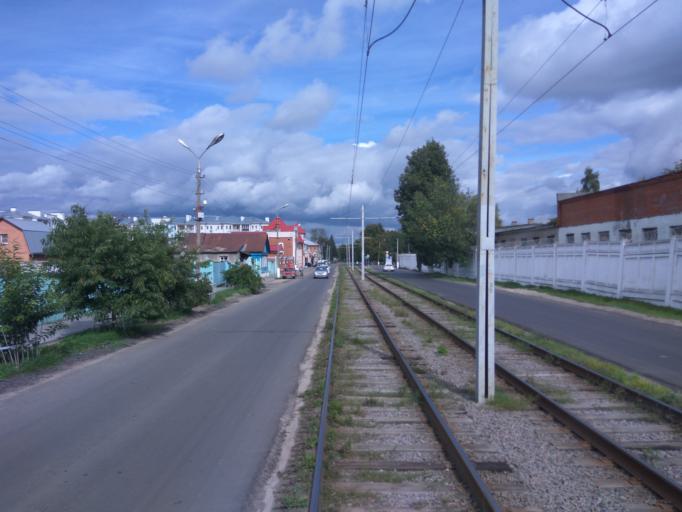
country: RU
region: Moskovskaya
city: Kolomna
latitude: 55.0976
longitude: 38.7738
